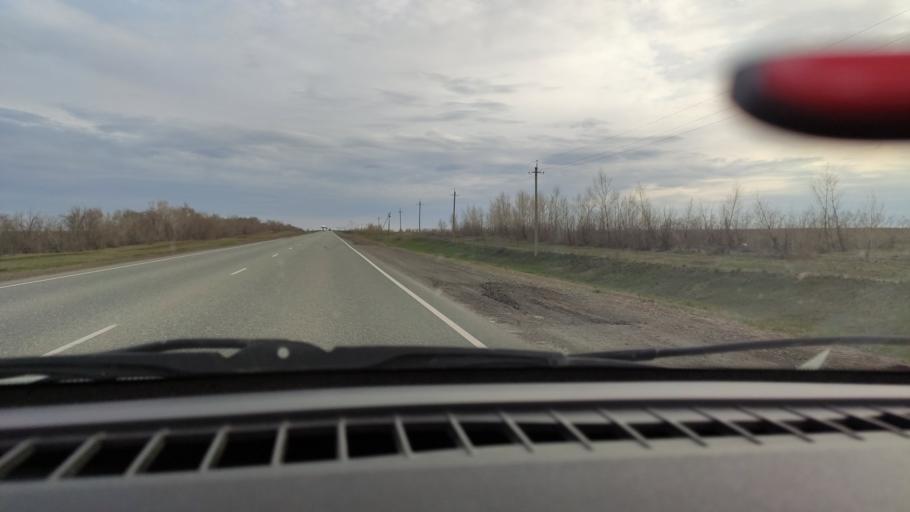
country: RU
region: Orenburg
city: Tatarskaya Kargala
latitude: 52.0091
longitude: 55.2026
